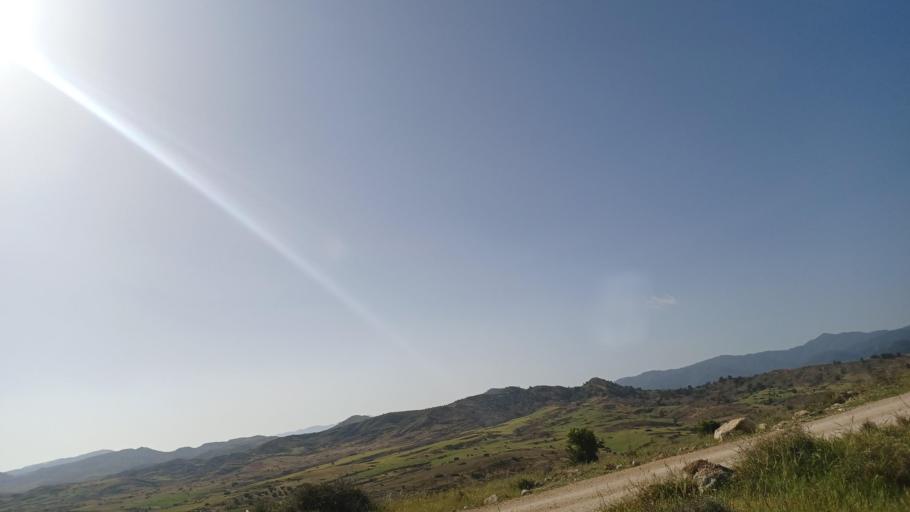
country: CY
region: Lefkosia
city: Astromeritis
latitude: 35.0847
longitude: 33.0263
